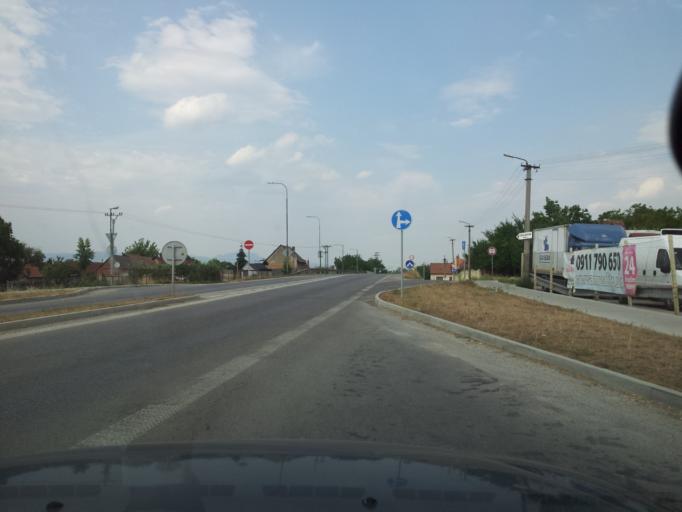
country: SK
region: Trenciansky
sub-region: Okres Trencin
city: Trencin
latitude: 48.9111
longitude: 18.0953
